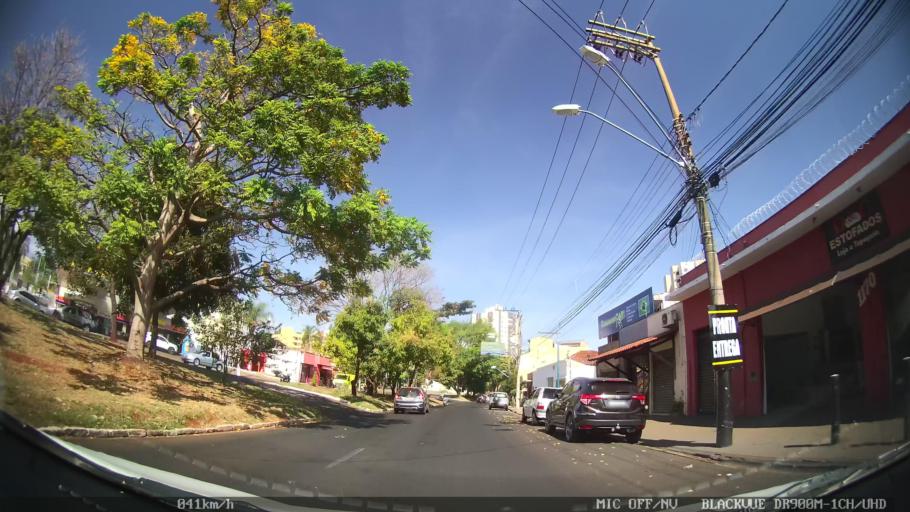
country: BR
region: Sao Paulo
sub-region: Ribeirao Preto
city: Ribeirao Preto
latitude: -21.1883
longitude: -47.8200
